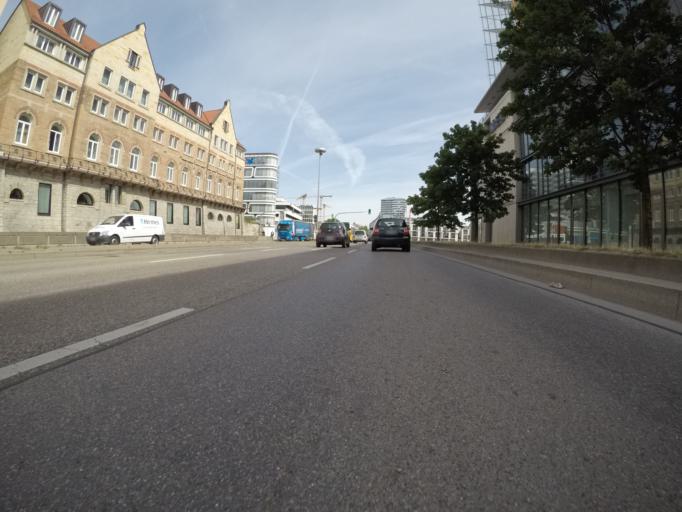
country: DE
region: Baden-Wuerttemberg
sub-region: Regierungsbezirk Stuttgart
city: Stuttgart
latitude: 48.7879
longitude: 9.1807
